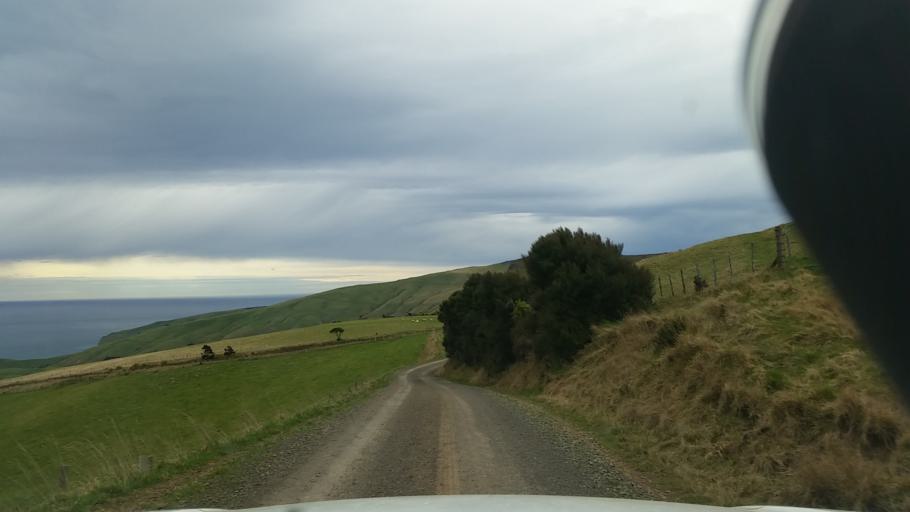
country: NZ
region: Canterbury
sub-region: Christchurch City
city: Christchurch
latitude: -43.8188
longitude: 173.0579
